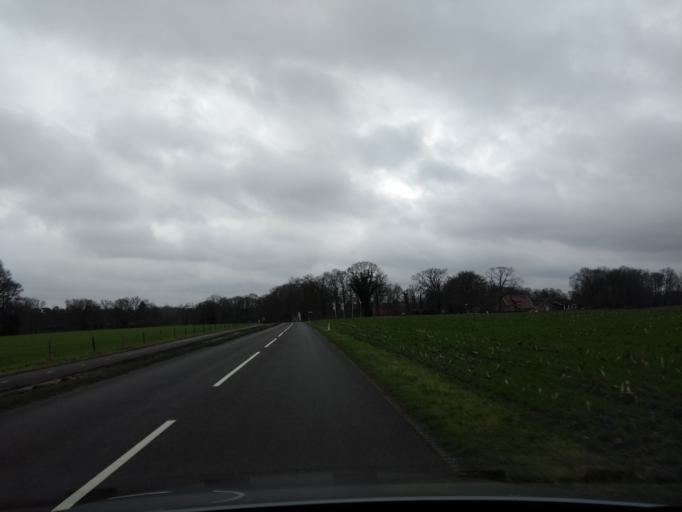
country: NL
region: Overijssel
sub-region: Gemeente Enschede
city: Enschede
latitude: 52.1420
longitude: 6.8453
